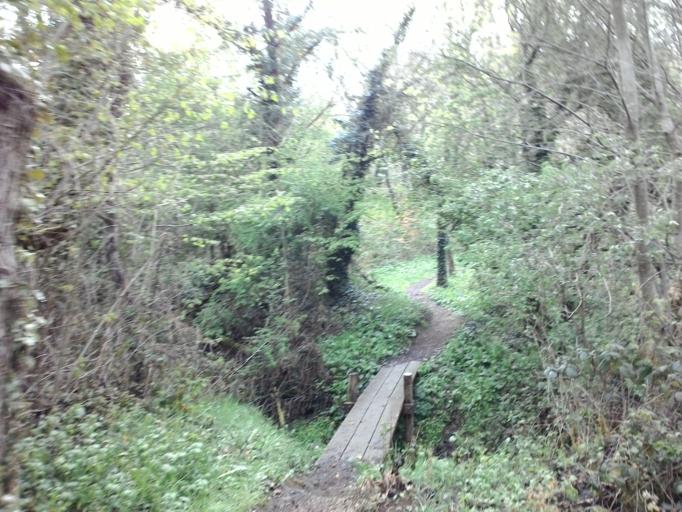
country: FR
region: Bourgogne
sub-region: Departement de la Cote-d'Or
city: Saulieu
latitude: 47.2481
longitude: 4.1953
